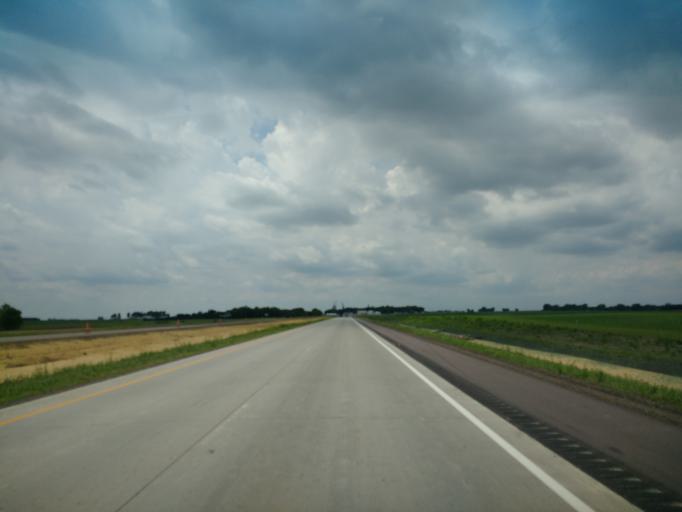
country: US
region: Minnesota
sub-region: Cottonwood County
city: Mountain Lake
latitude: 43.9127
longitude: -95.0224
